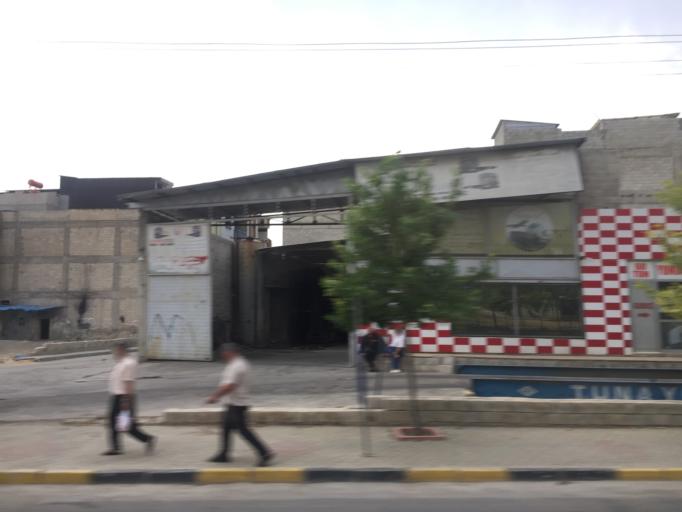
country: TR
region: Gaziantep
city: Gaziantep
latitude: 37.0631
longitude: 37.4154
